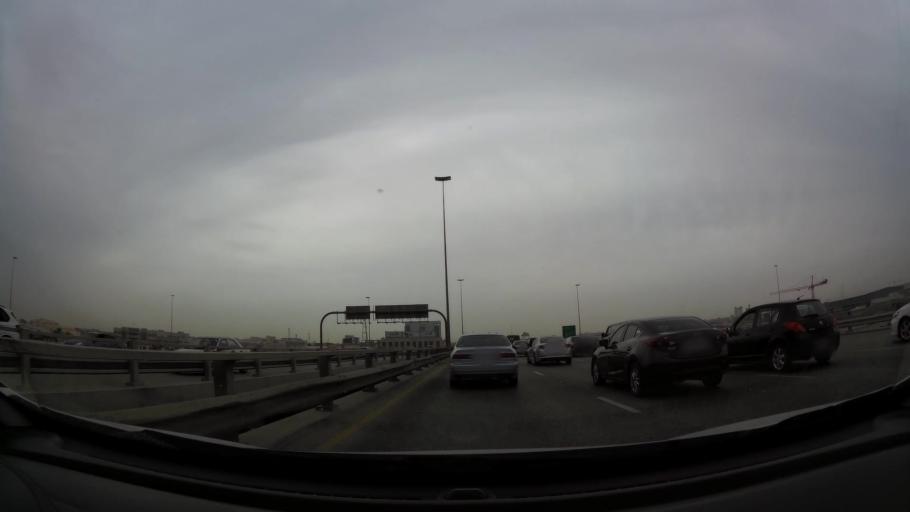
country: BH
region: Northern
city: Madinat `Isa
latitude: 26.1957
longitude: 50.5346
